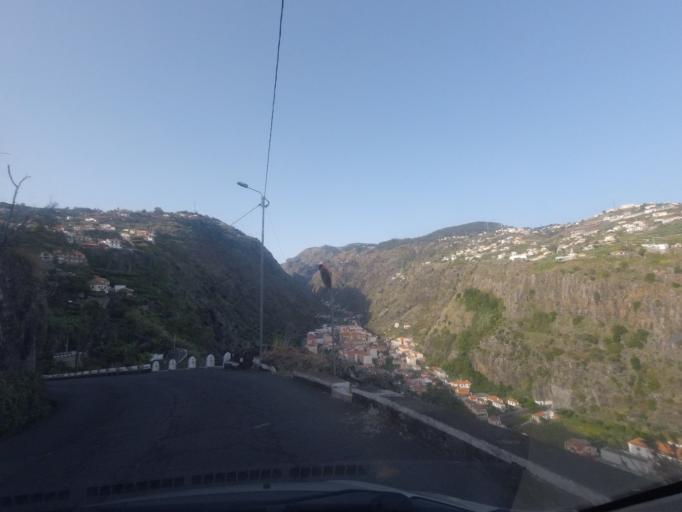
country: PT
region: Madeira
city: Ribeira Brava
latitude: 32.6736
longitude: -17.0658
